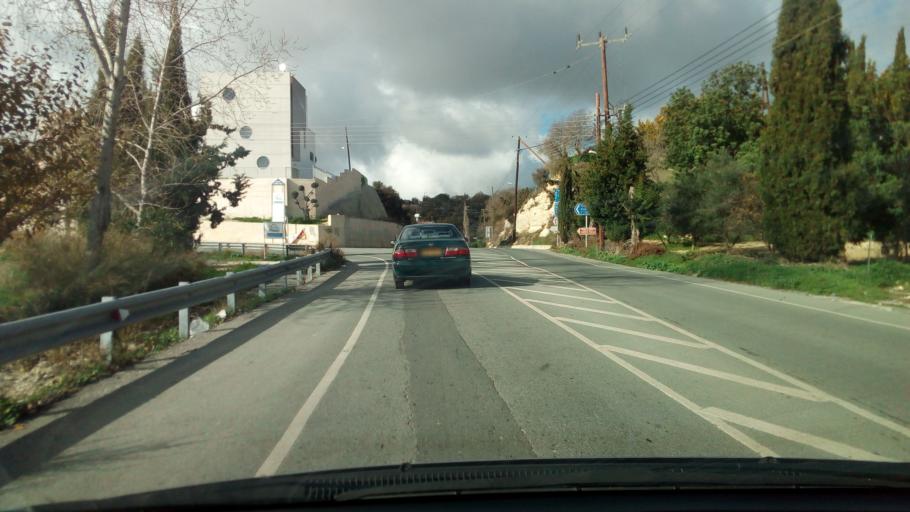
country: CY
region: Pafos
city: Mesogi
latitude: 34.8419
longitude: 32.4680
